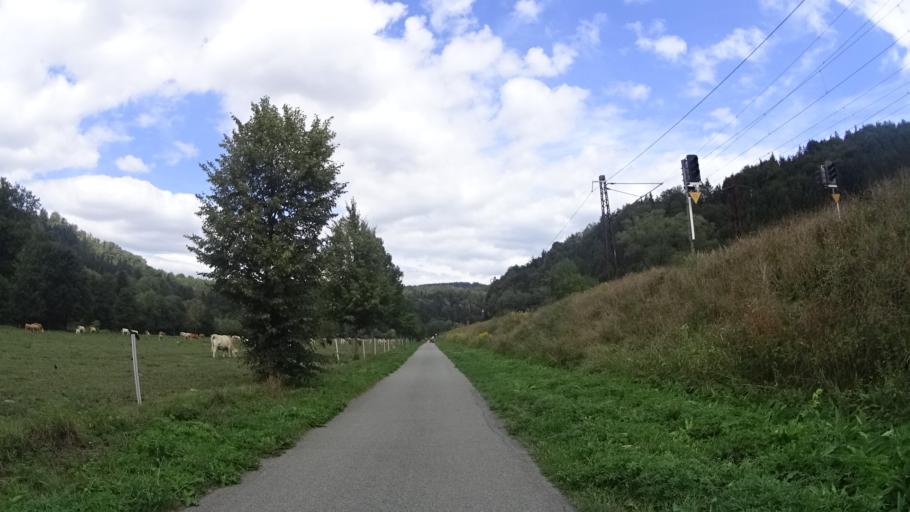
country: CZ
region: Pardubicky
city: Brandys nad Orlici
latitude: 49.9842
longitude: 16.3358
